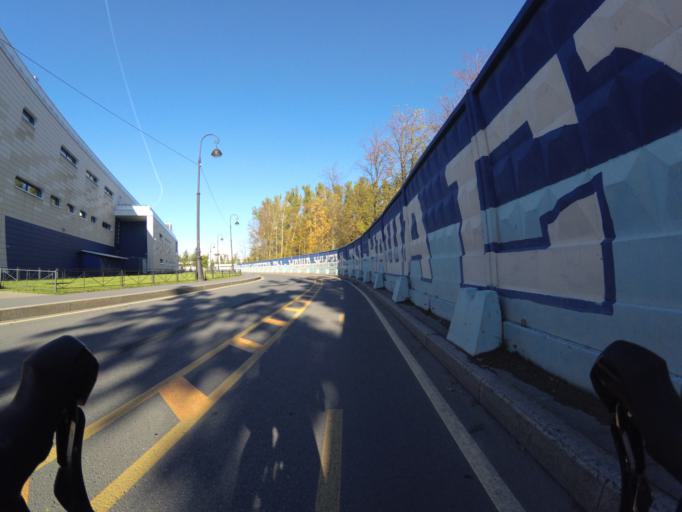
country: RU
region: St.-Petersburg
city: Staraya Derevnya
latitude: 59.9709
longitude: 30.2314
